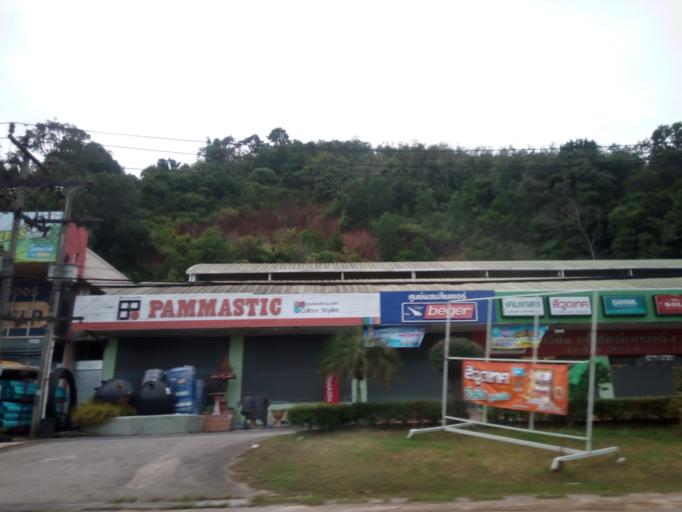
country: TH
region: Phuket
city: Wichit
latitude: 7.9143
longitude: 98.3678
